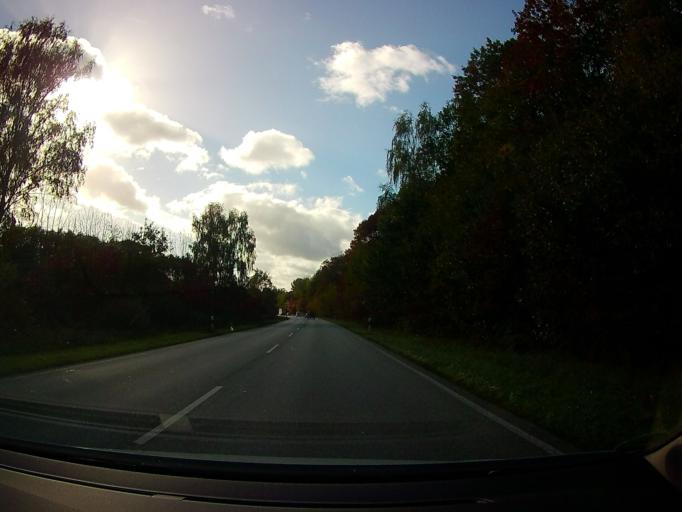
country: DE
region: Schleswig-Holstein
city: Gronwohld
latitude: 53.6426
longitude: 10.3933
